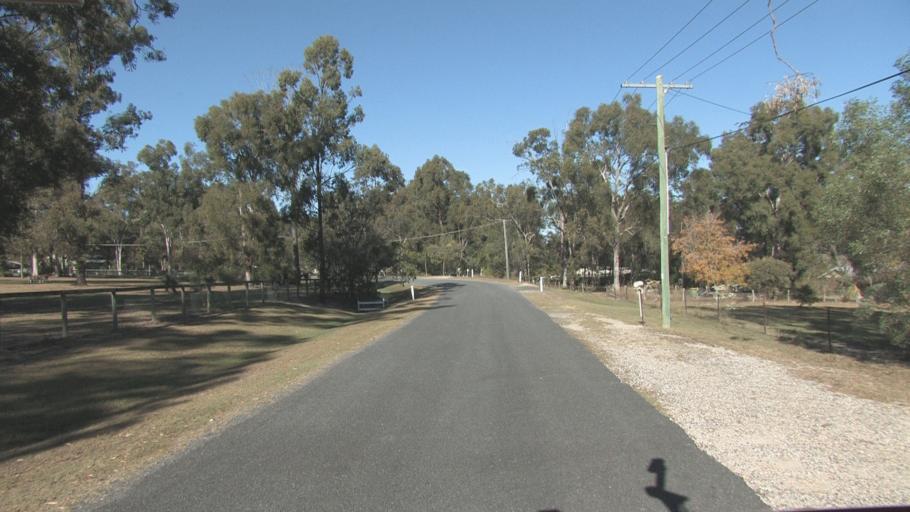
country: AU
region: Queensland
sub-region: Logan
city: Chambers Flat
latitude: -27.7910
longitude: 153.1289
